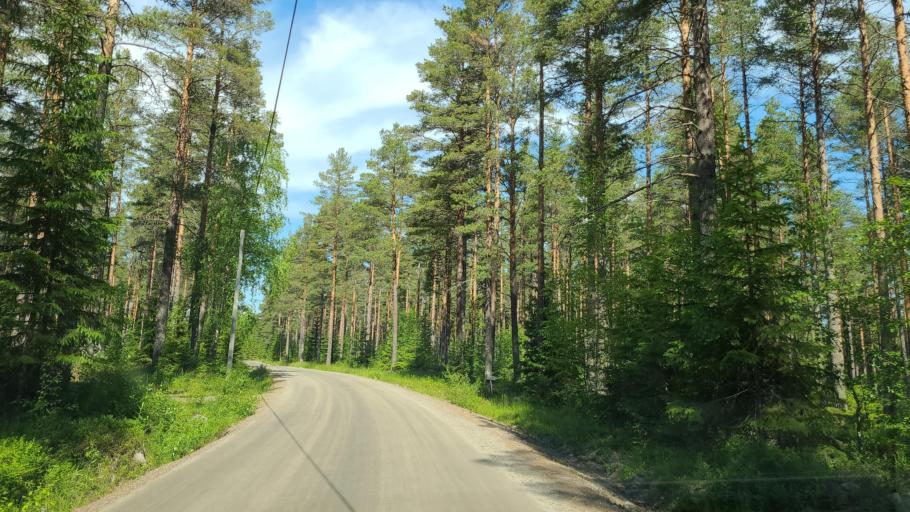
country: SE
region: Vaesterbotten
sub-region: Robertsfors Kommun
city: Robertsfors
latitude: 64.1493
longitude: 20.9539
